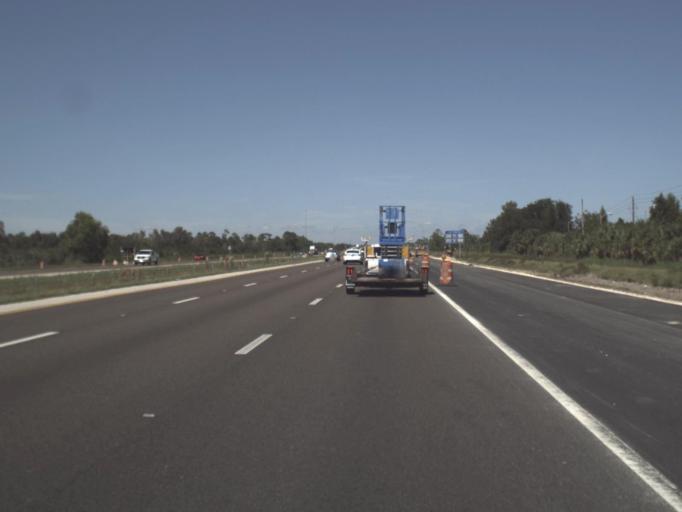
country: US
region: Florida
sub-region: Lee County
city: Gateway
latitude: 26.5360
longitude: -81.7947
